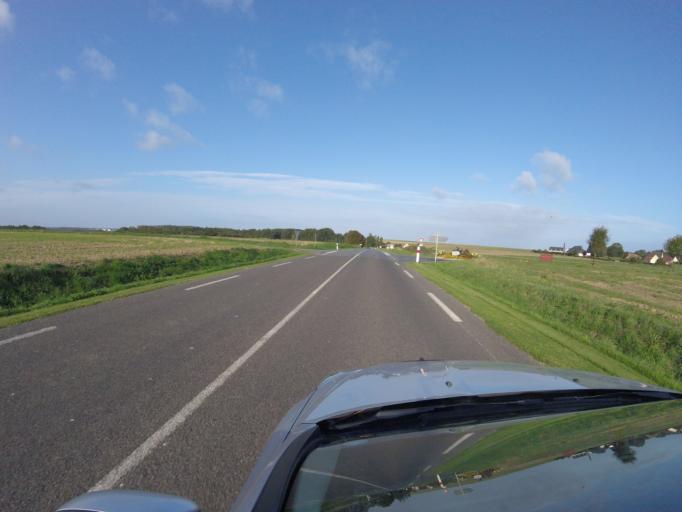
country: FR
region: Haute-Normandie
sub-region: Departement de la Seine-Maritime
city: Fecamp
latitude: 49.7677
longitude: 0.4109
